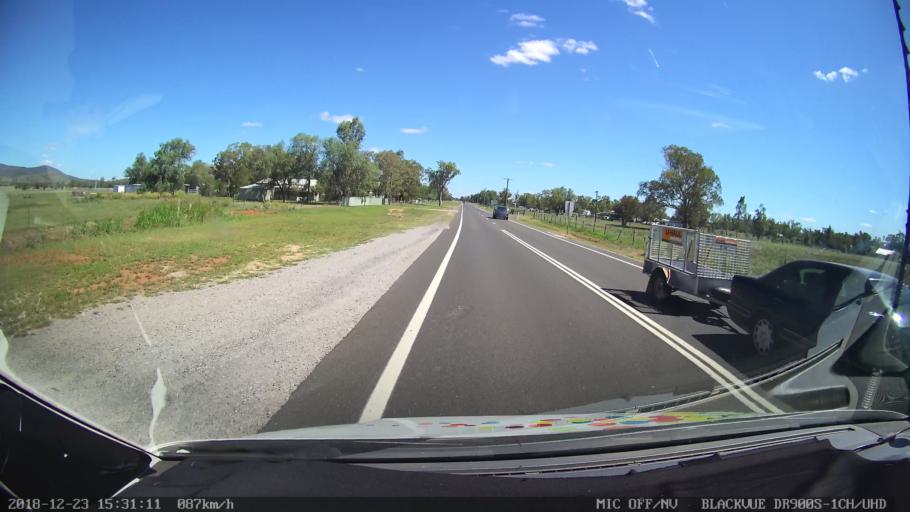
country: AU
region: New South Wales
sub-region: Tamworth Municipality
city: East Tamworth
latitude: -30.9687
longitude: 150.8666
